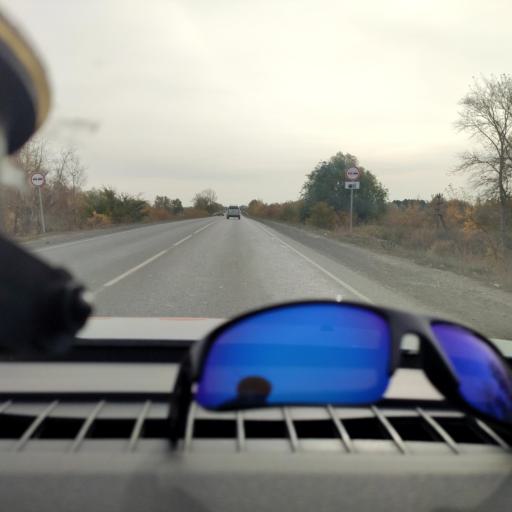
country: RU
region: Samara
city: Samara
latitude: 53.1045
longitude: 50.1371
